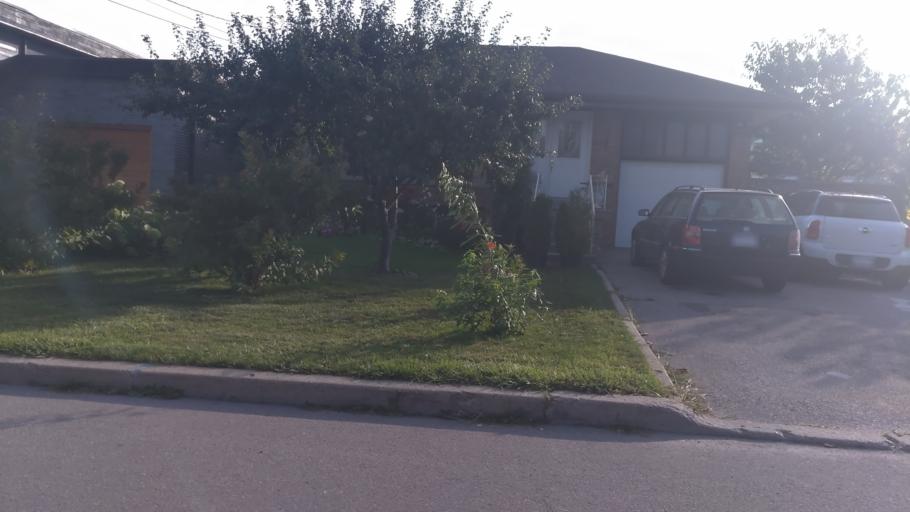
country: CA
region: Ontario
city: Toronto
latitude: 43.7229
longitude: -79.4510
